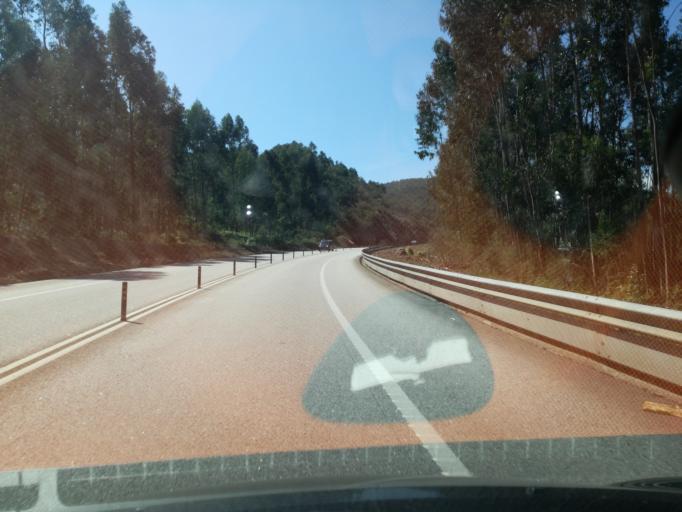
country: PT
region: Viana do Castelo
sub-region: Vila Nova de Cerveira
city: Vila Nova de Cerveira
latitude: 41.8923
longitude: -8.7727
